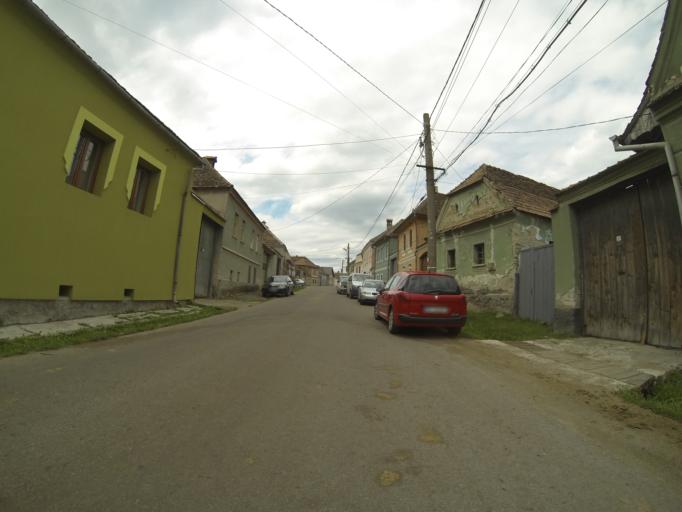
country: RO
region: Brasov
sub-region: Comuna Hoghiz
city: Hoghiz
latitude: 46.0250
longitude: 25.4033
